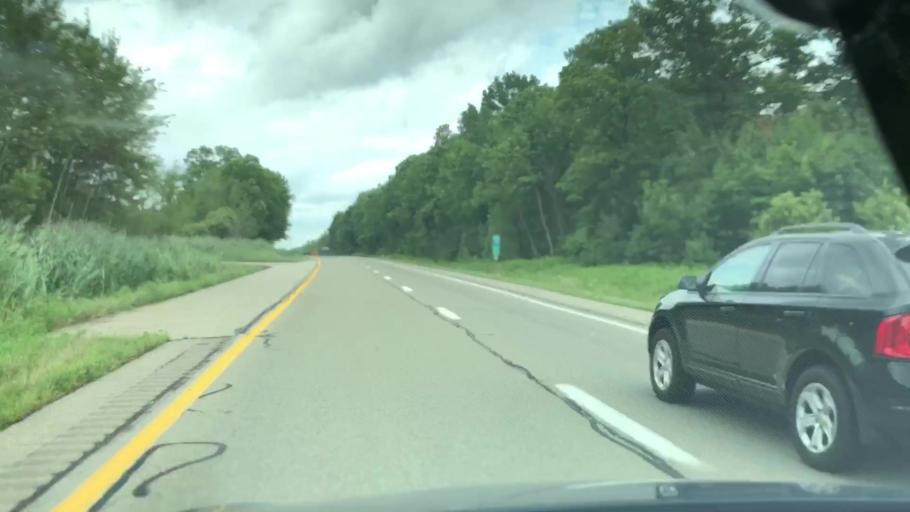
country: US
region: Pennsylvania
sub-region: Erie County
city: Edinboro
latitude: 41.8267
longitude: -80.1749
